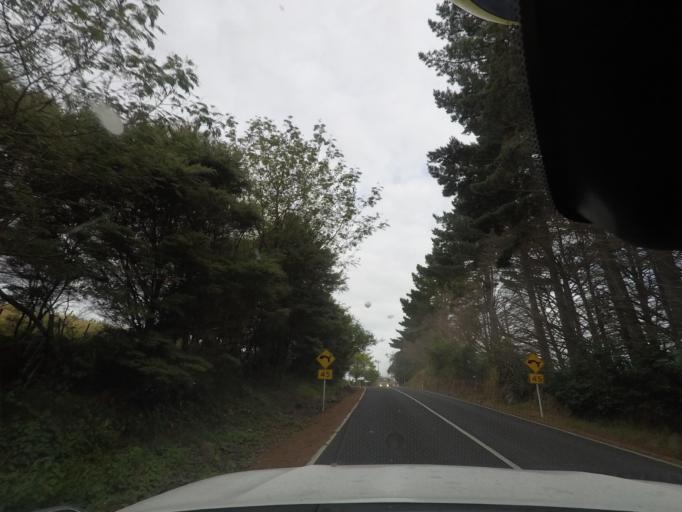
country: NZ
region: Auckland
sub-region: Auckland
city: Parakai
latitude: -36.5217
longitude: 174.2726
